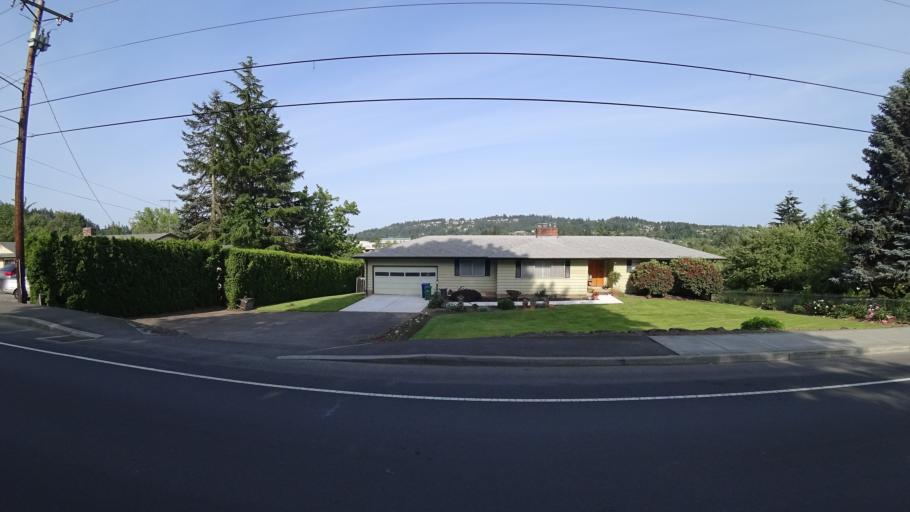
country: US
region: Oregon
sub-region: Clackamas County
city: Happy Valley
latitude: 45.4486
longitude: -122.5144
